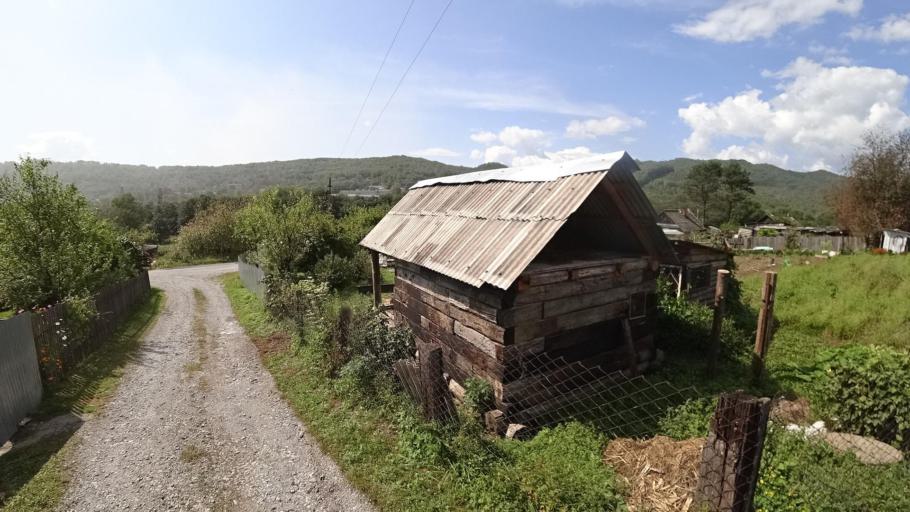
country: RU
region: Jewish Autonomous Oblast
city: Londoko
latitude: 49.0285
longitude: 131.9304
